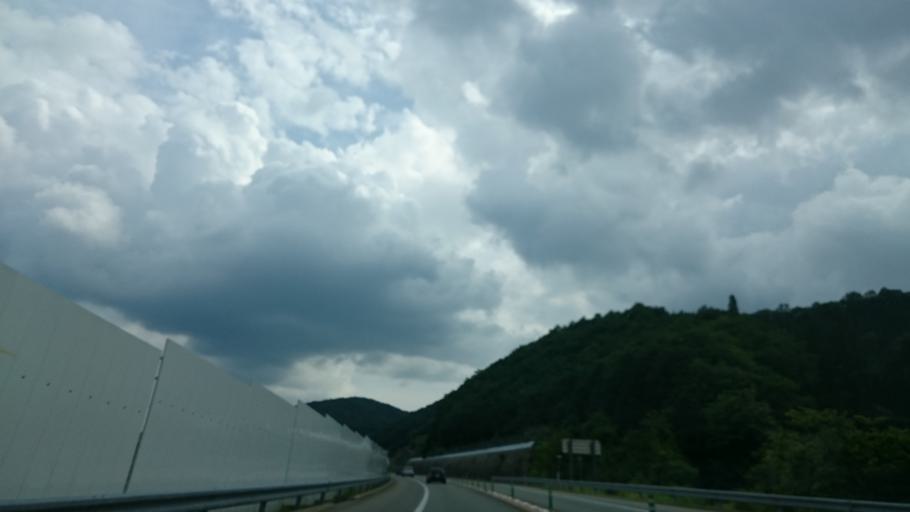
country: JP
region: Gifu
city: Takayama
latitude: 36.1037
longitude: 137.0737
